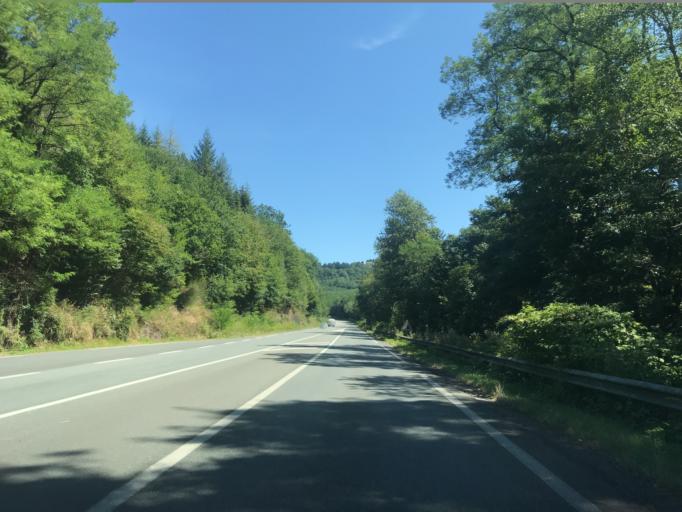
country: FR
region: Limousin
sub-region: Departement de la Correze
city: Cornil
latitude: 45.2059
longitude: 1.6754
